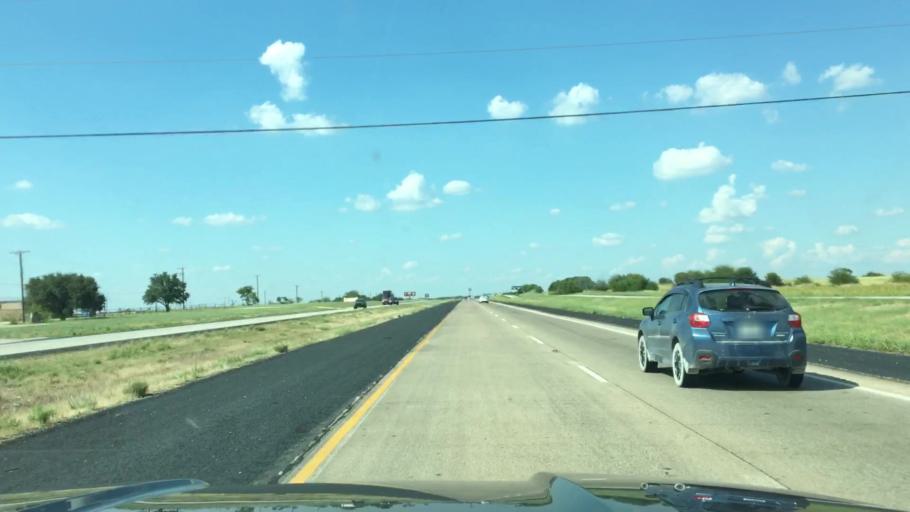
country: US
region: Texas
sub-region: Wise County
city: Rhome
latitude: 33.0803
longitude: -97.4725
